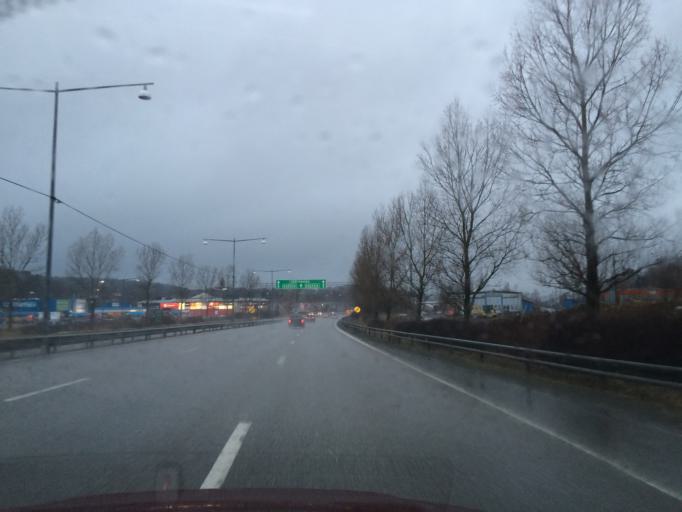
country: SE
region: Vaestra Goetaland
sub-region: Molndal
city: Kallered
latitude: 57.6045
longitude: 12.0510
